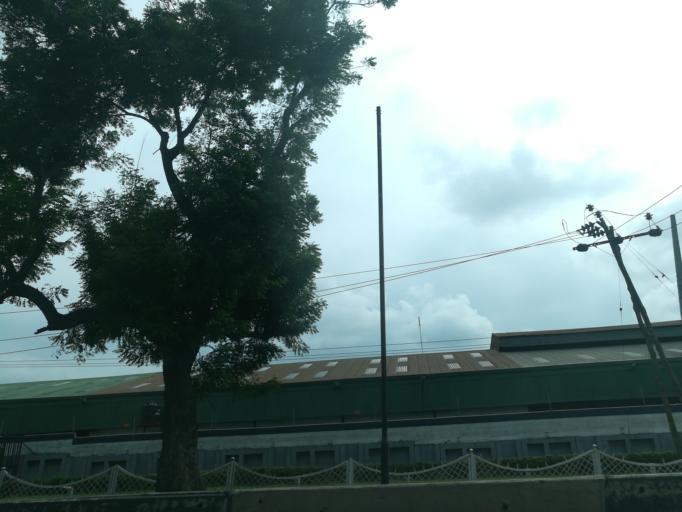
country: NG
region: Lagos
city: Ojota
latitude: 6.6015
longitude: 3.3738
